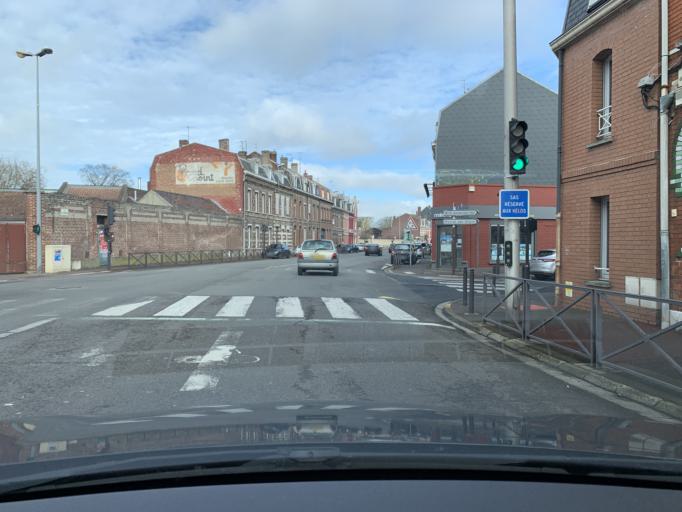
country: FR
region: Nord-Pas-de-Calais
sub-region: Departement du Nord
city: Douai
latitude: 50.3616
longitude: 3.0785
